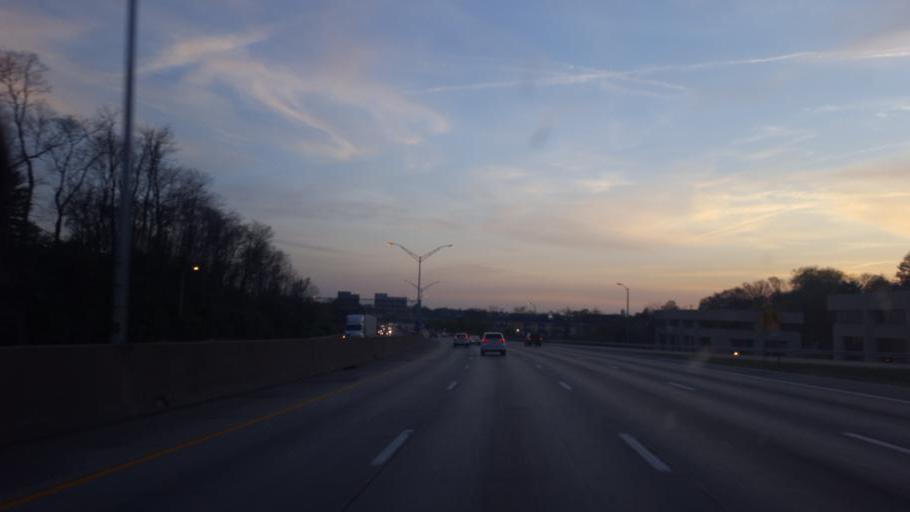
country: US
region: Kentucky
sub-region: Kenton County
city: Fort Mitchell
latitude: 39.0582
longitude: -84.5407
